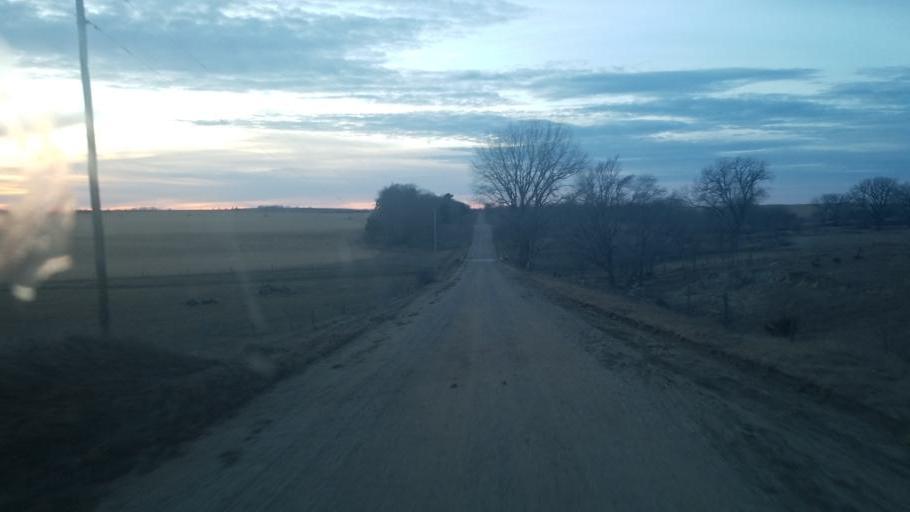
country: US
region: Nebraska
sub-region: Knox County
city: Center
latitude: 42.6554
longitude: -97.7685
